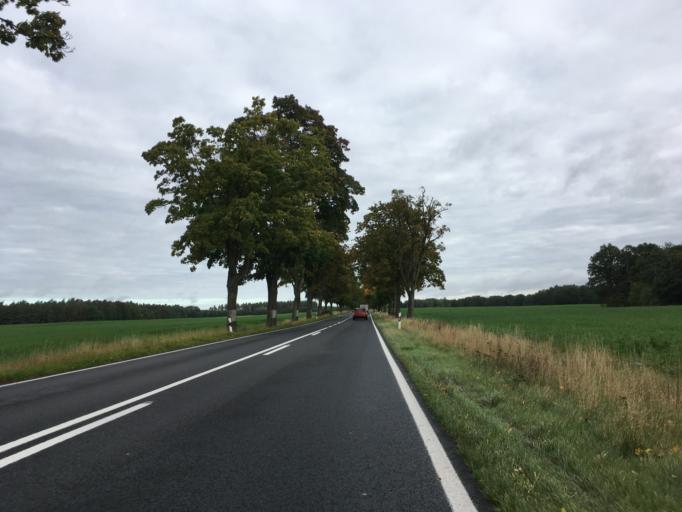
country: DE
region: Brandenburg
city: Werftpfuhl
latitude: 52.6929
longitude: 13.8634
